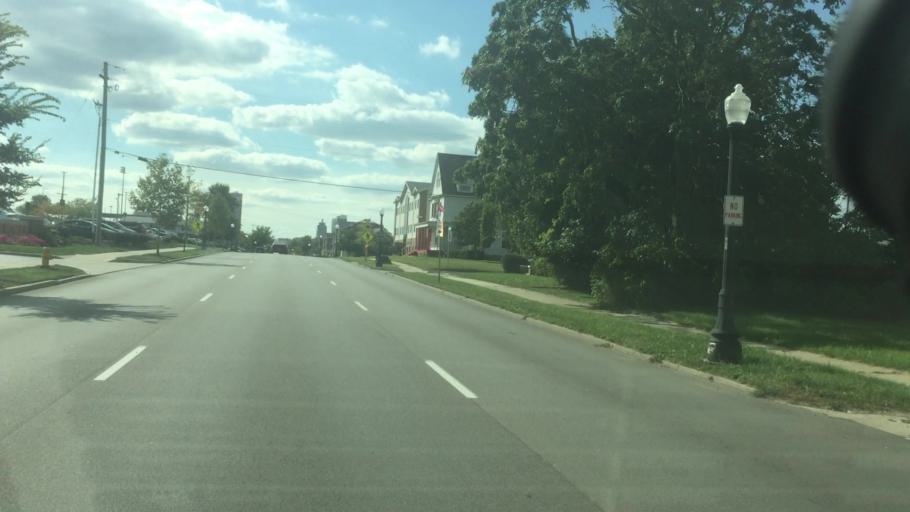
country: US
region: Indiana
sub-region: Allen County
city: Fort Wayne
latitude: 41.0791
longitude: -85.1165
